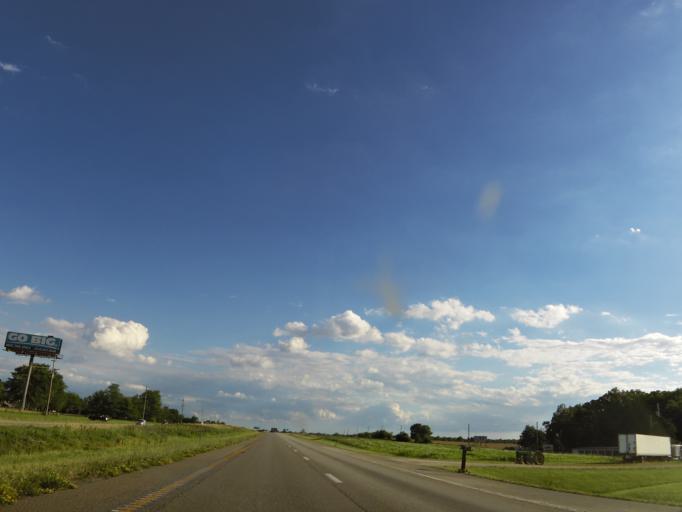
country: US
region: Missouri
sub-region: Lincoln County
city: Troy
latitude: 39.0911
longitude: -90.9689
